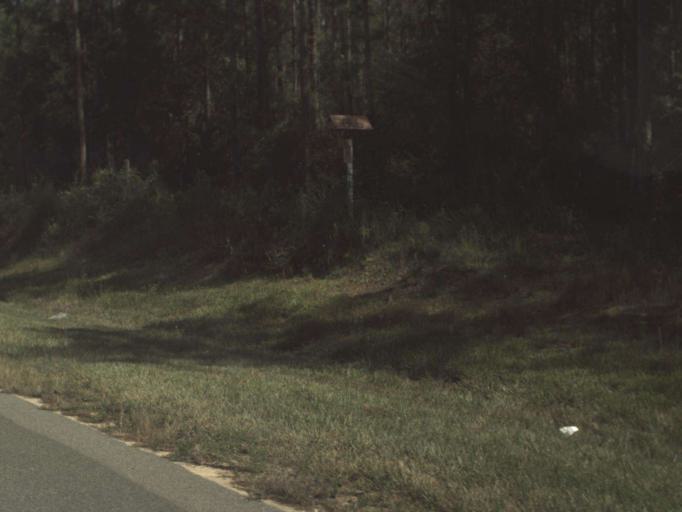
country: US
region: Florida
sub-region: Washington County
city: Chipley
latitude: 30.6659
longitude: -85.5760
